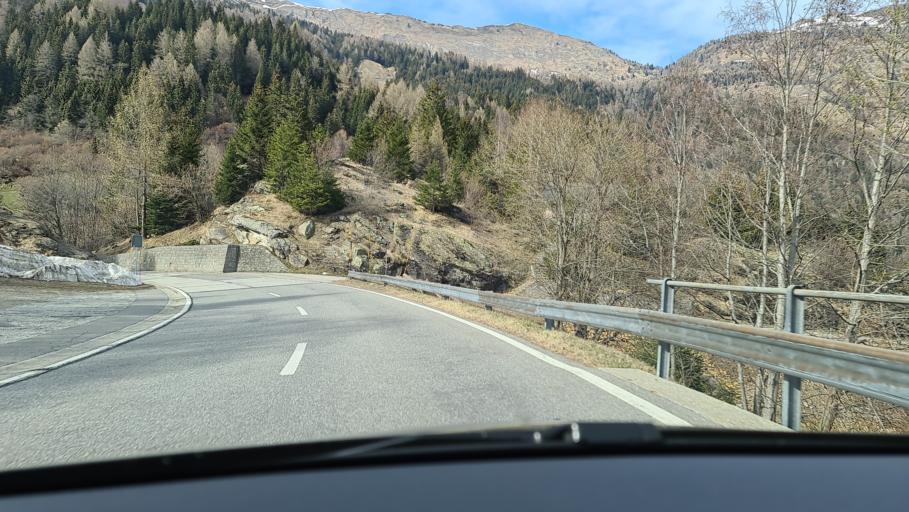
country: CH
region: Ticino
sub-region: Blenio District
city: Cancori
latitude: 46.5237
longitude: 8.9008
